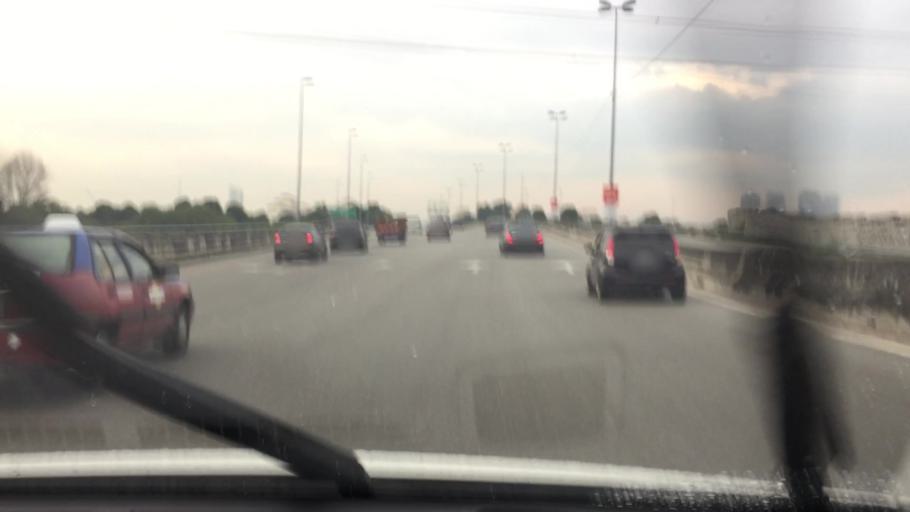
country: MY
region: Selangor
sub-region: Petaling
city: Petaling Jaya
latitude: 3.0721
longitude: 101.6417
